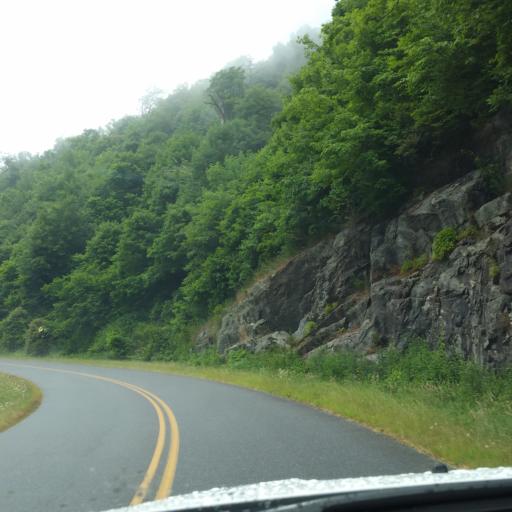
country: US
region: North Carolina
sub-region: Transylvania County
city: Brevard
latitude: 35.3812
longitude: -82.7863
